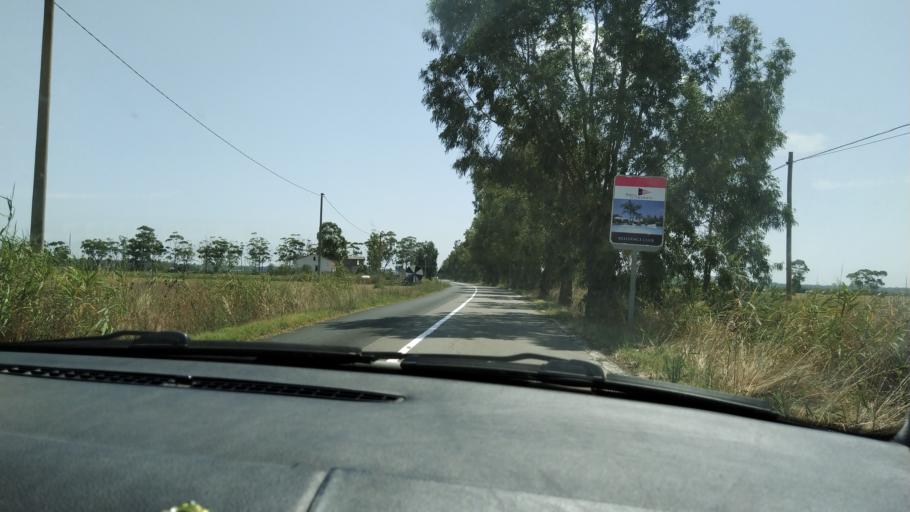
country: IT
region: Basilicate
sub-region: Provincia di Matera
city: Marconia
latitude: 40.3339
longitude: 16.7766
